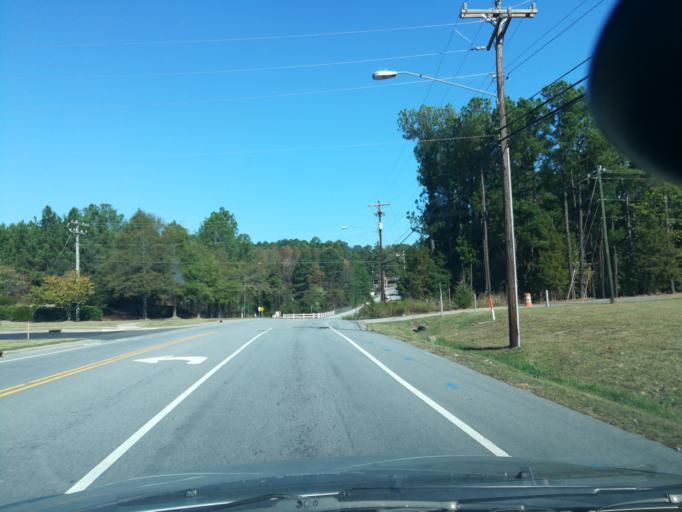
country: US
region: North Carolina
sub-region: Durham County
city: Durham
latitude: 36.0329
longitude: -78.9108
